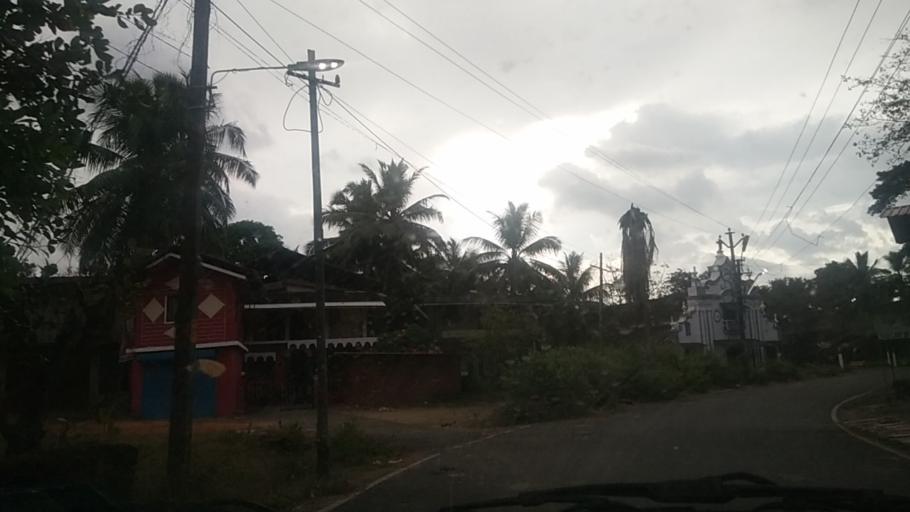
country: IN
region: Goa
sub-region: South Goa
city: Chinchinim
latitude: 15.2015
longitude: 73.9777
